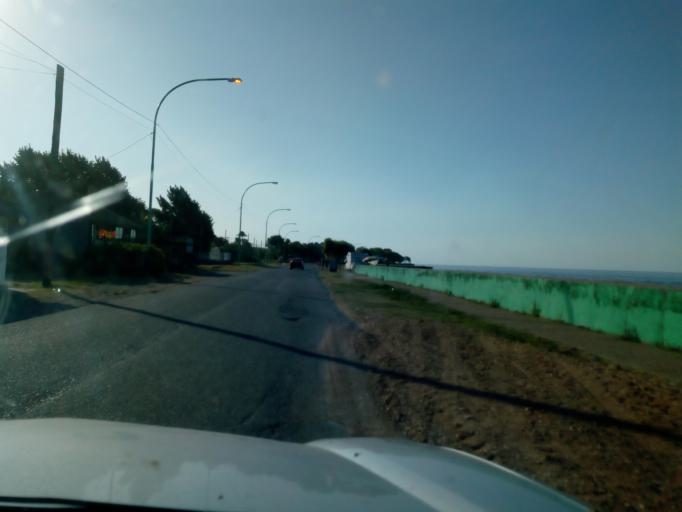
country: AR
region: Buenos Aires
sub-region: Partido de Ensenada
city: Ensenada
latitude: -34.7968
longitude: -57.9926
